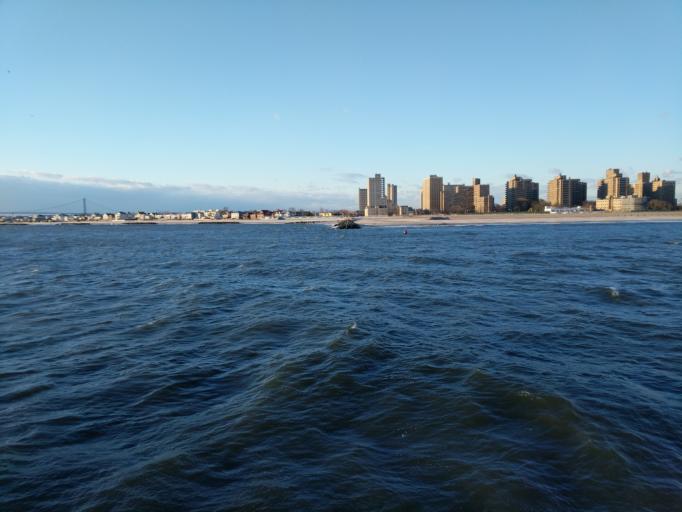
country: US
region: New York
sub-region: Kings County
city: Coney Island
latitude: 40.5675
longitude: -74.0017
